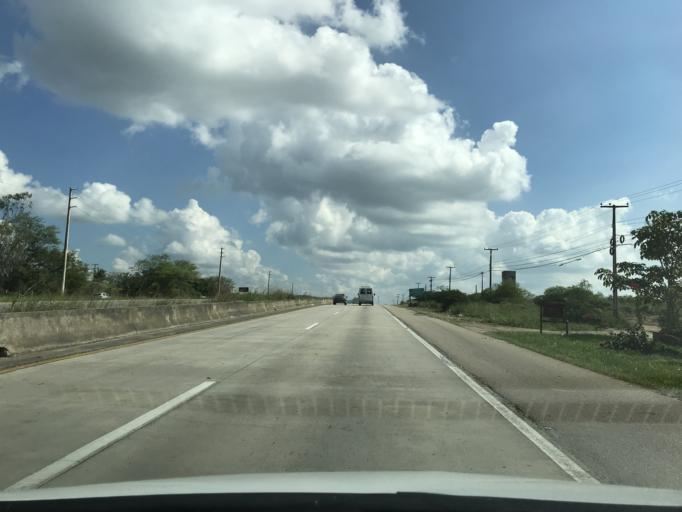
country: BR
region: Pernambuco
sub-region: Gravata
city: Gravata
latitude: -8.2053
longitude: -35.6018
